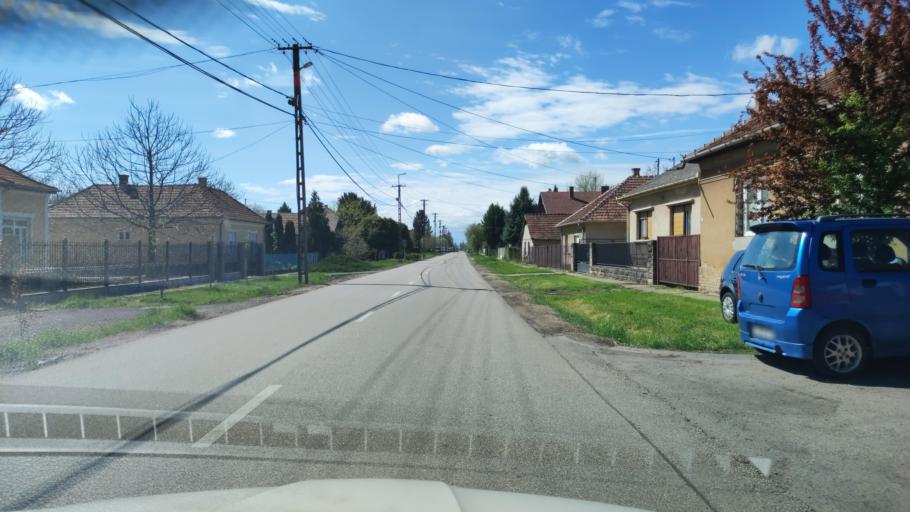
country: HU
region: Pest
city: Abony
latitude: 47.1808
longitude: 20.0060
